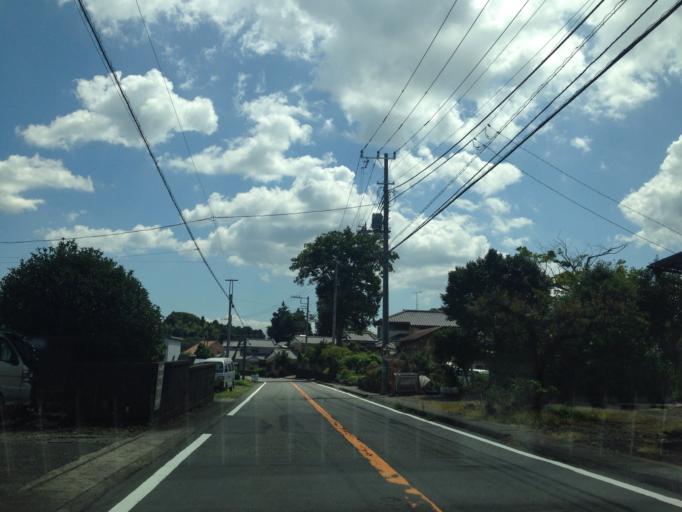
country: JP
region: Shizuoka
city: Mishima
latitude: 35.2088
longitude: 138.9013
